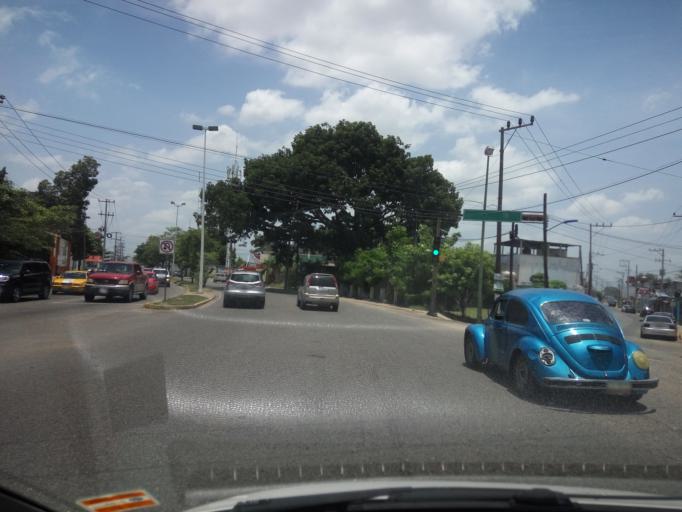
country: MX
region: Tabasco
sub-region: Nacajuca
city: Bosque de Saloya
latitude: 17.9923
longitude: -92.9612
